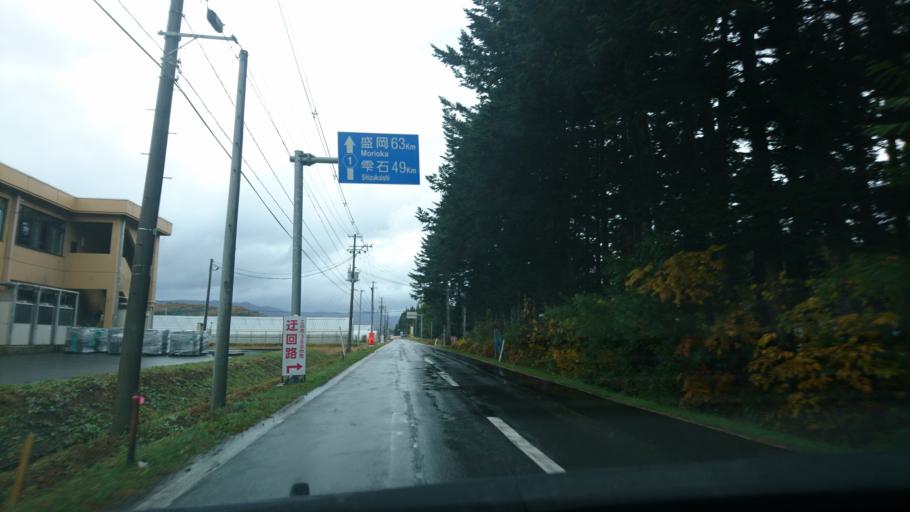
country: JP
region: Akita
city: Yokotemachi
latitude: 39.3741
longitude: 140.7604
